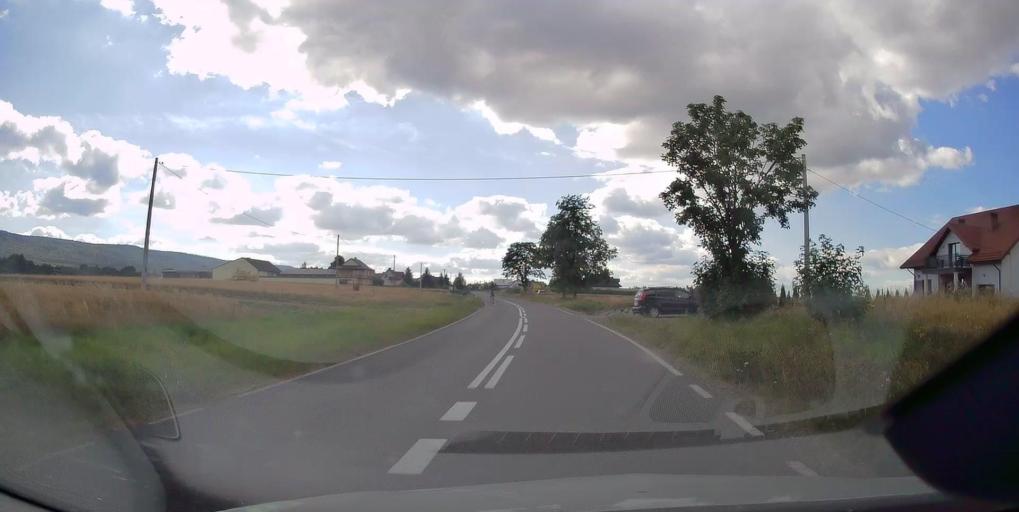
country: PL
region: Swietokrzyskie
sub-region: Powiat kielecki
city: Nowa Slupia
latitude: 50.8925
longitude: 21.0367
